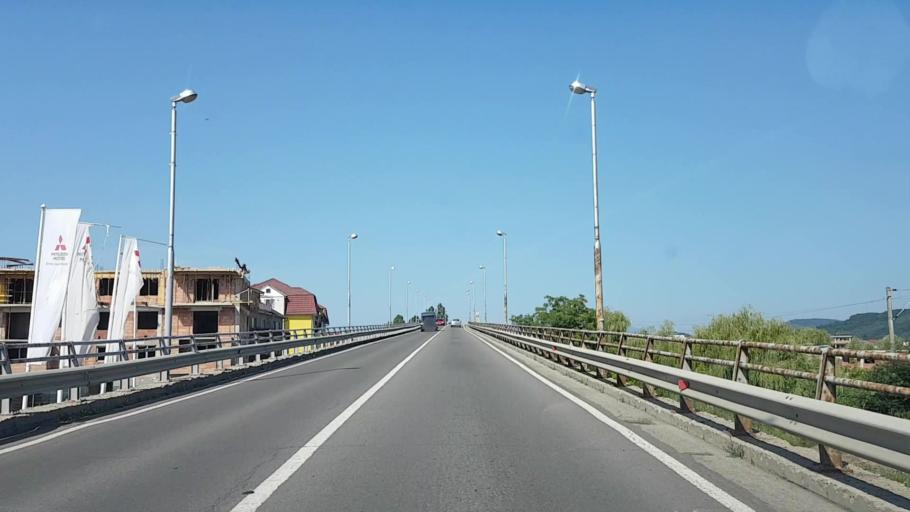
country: RO
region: Bistrita-Nasaud
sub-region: Municipiul Bistrita
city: Viisoara
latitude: 47.1152
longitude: 24.4645
